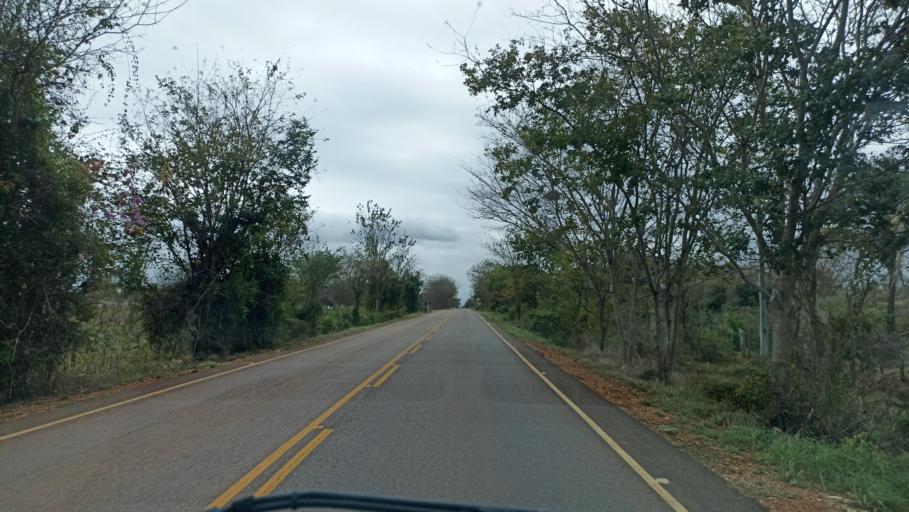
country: BR
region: Bahia
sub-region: Andarai
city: Vera Cruz
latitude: -12.9791
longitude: -41.0169
